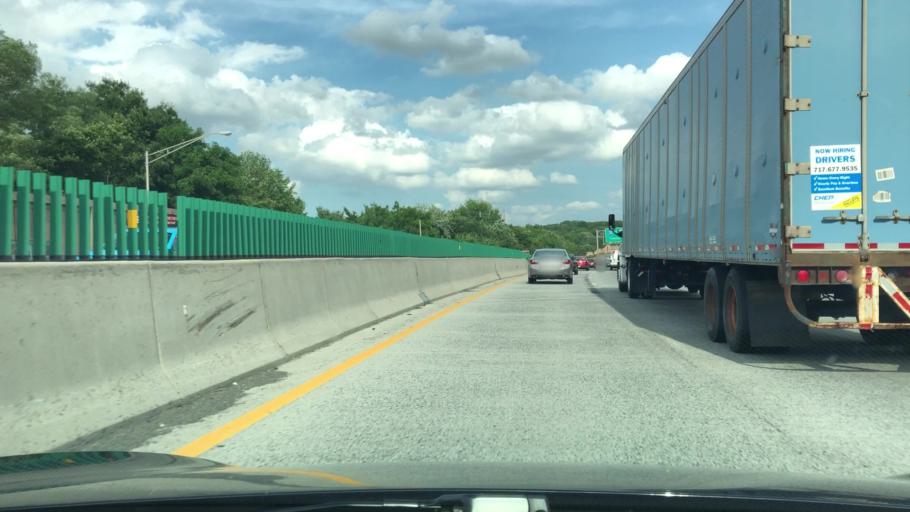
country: US
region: New Jersey
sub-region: Camden County
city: Barrington
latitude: 39.8752
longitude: -75.0524
